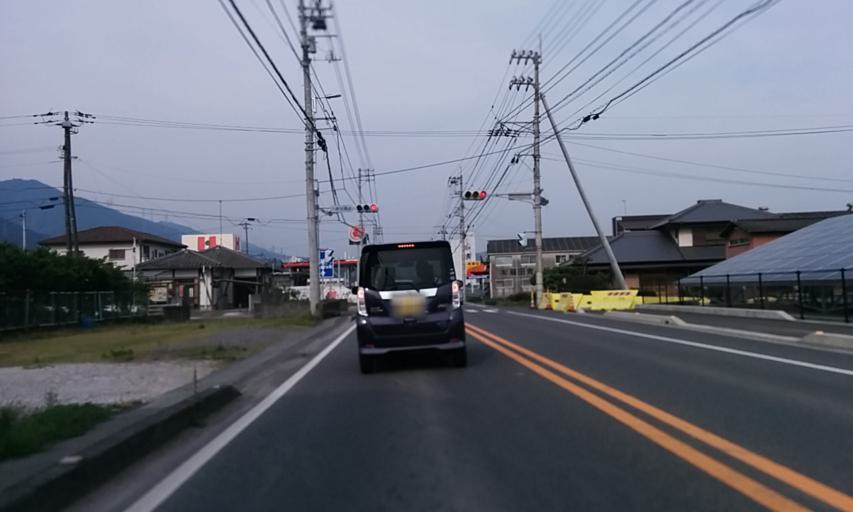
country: JP
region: Ehime
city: Niihama
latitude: 33.9551
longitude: 133.4220
